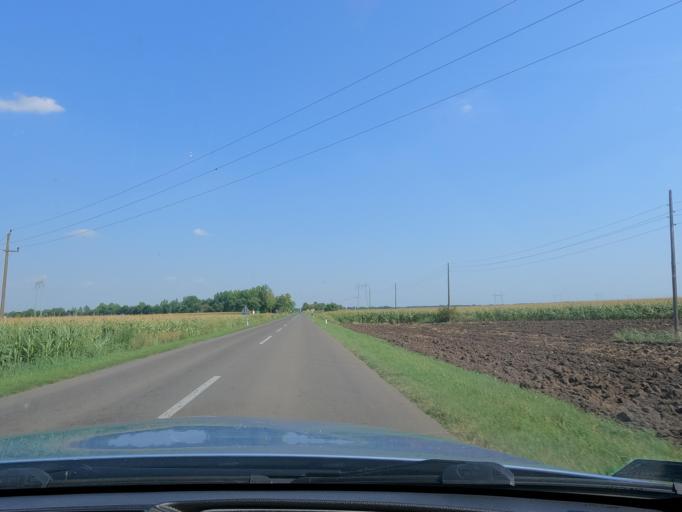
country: RS
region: Autonomna Pokrajina Vojvodina
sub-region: Severnobacki Okrug
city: Mali Igos
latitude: 45.7510
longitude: 19.7909
